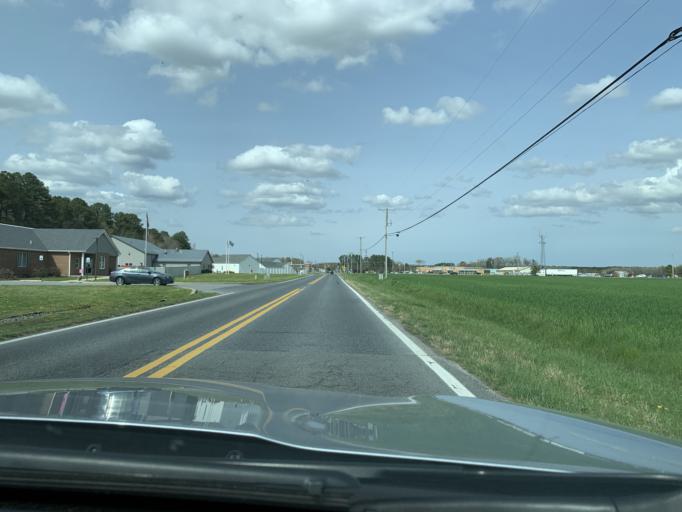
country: US
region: Delaware
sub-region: Sussex County
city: Georgetown
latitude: 38.6607
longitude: -75.3798
